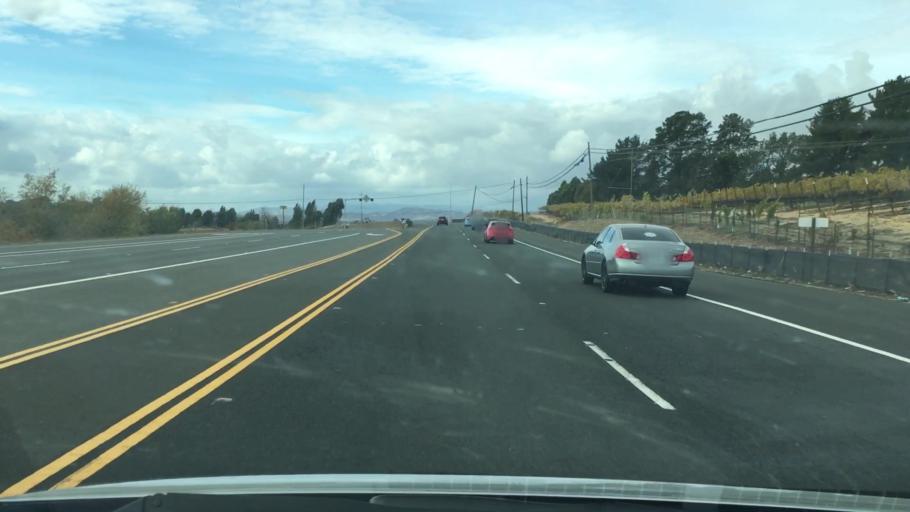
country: US
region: California
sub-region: Napa County
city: American Canyon
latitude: 38.2207
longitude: -122.2354
